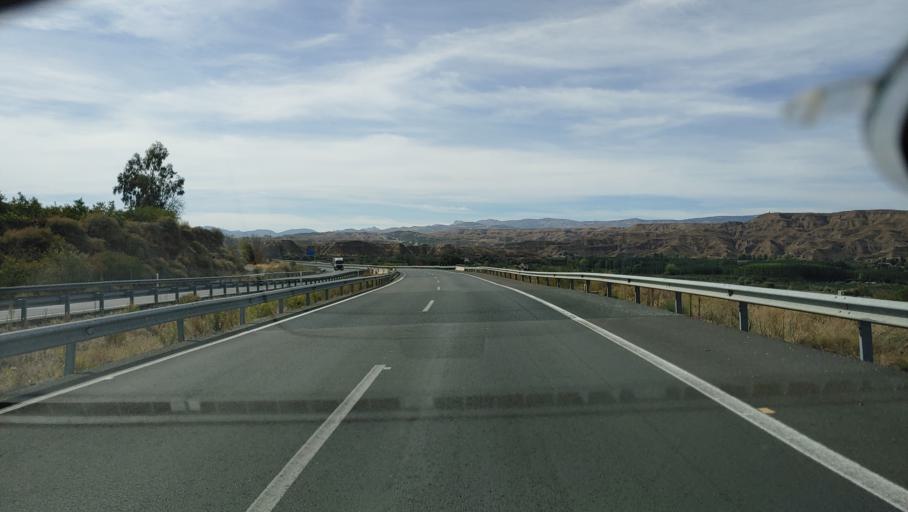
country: ES
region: Andalusia
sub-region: Provincia de Granada
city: Purullena
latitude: 37.3283
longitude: -3.1838
